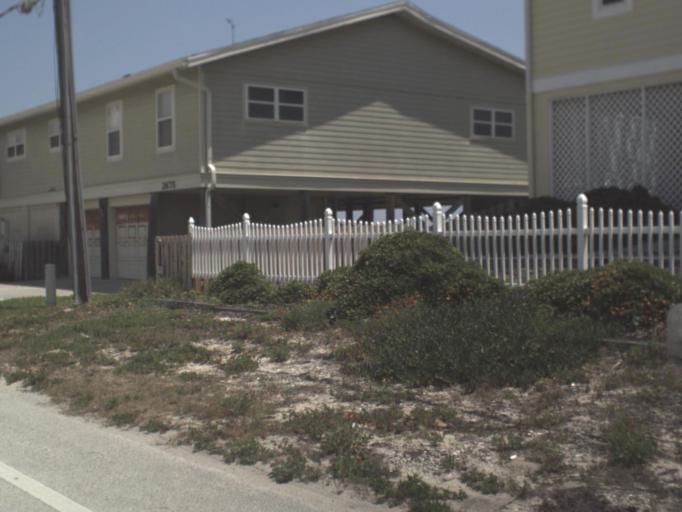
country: US
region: Florida
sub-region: Saint Johns County
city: Villano Beach
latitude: 30.0255
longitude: -81.3240
